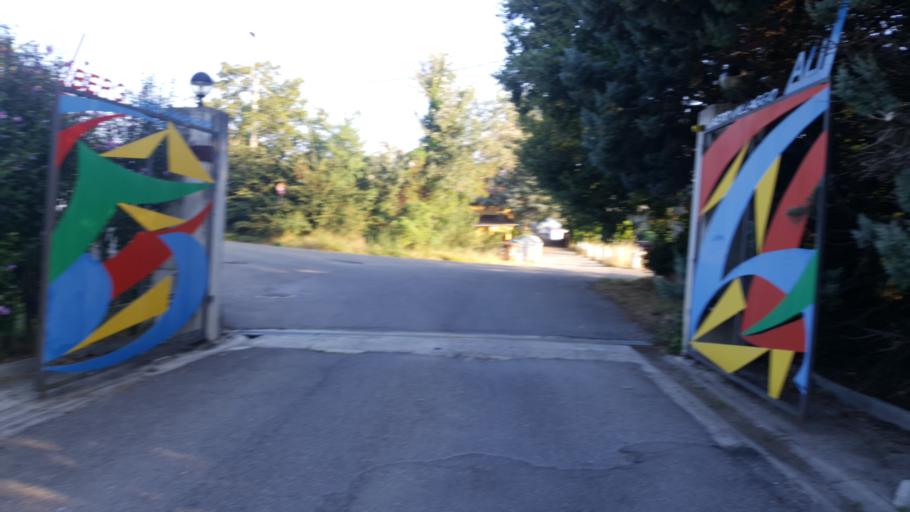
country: IT
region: Lombardy
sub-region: Provincia di Pavia
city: Retorbido
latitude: 44.9527
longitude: 9.0147
